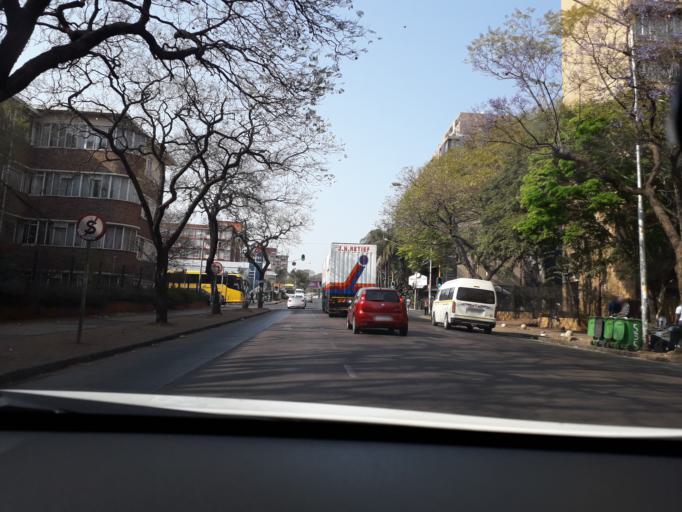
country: ZA
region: Gauteng
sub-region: City of Tshwane Metropolitan Municipality
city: Pretoria
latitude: -25.7560
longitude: 28.1913
